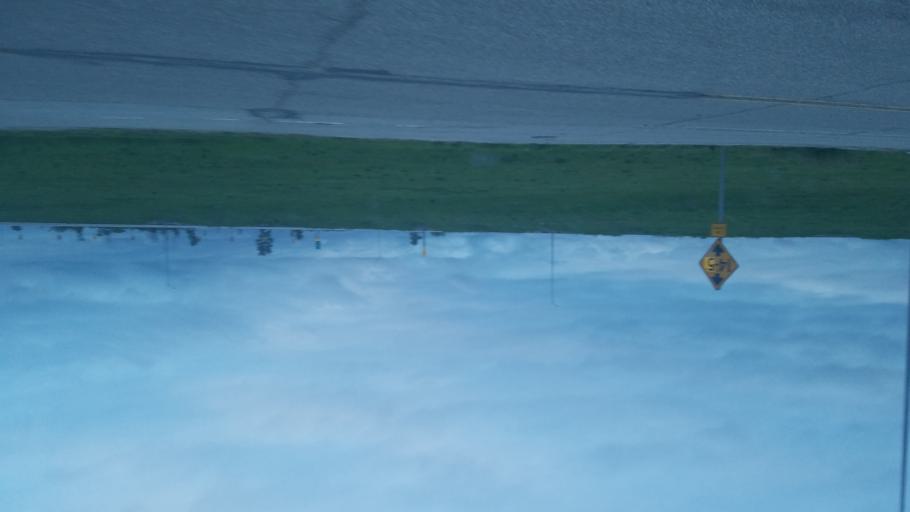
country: US
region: Iowa
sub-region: Decatur County
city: Lamoni
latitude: 40.5753
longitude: -93.9398
